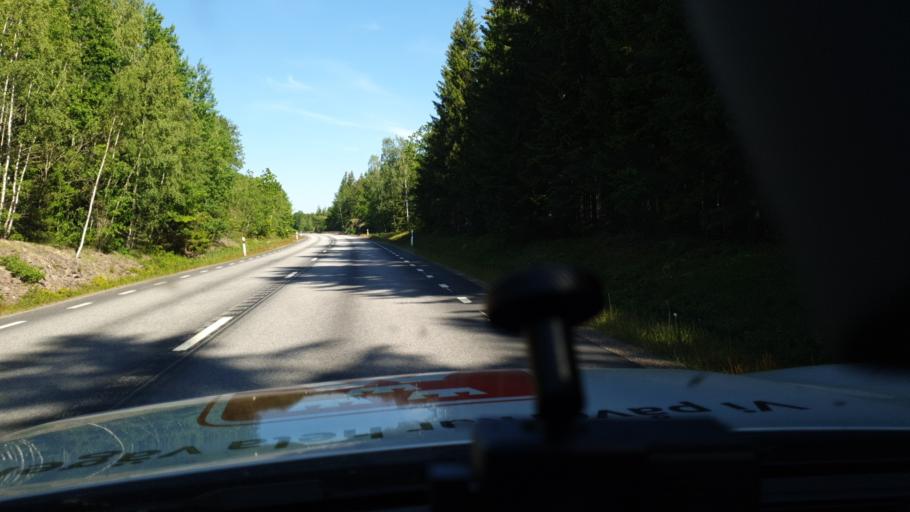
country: SE
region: Kalmar
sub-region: Vasterviks Kommun
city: Ankarsrum
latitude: 57.7088
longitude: 16.1305
